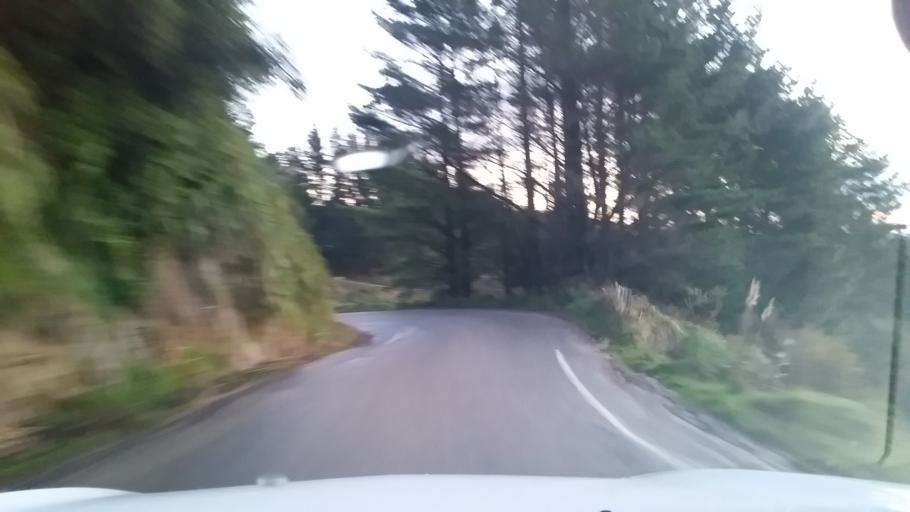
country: NZ
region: Manawatu-Wanganui
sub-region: Wanganui District
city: Wanganui
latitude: -39.7759
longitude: 174.8586
